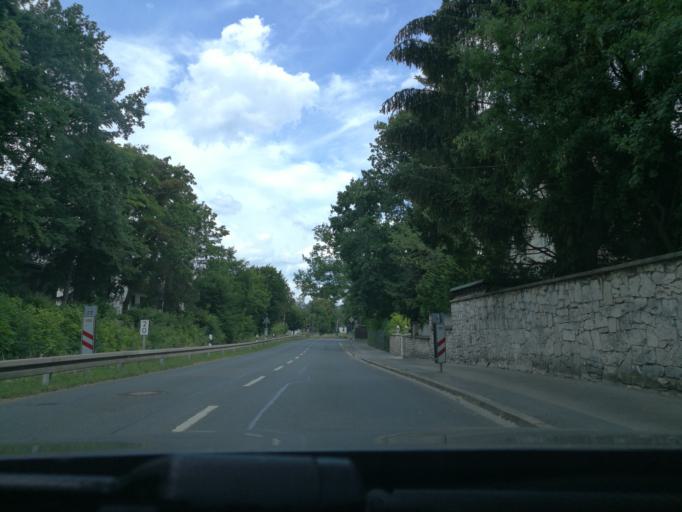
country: DE
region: Bavaria
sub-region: Regierungsbezirk Mittelfranken
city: Furth
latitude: 49.4649
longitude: 10.9701
